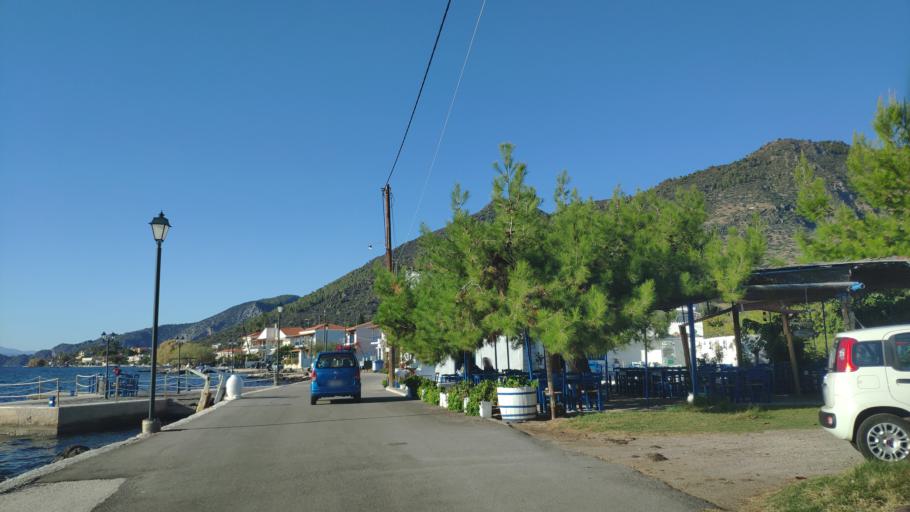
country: GR
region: Attica
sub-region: Nomos Piraios
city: Megalochori
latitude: 37.5859
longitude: 23.3482
